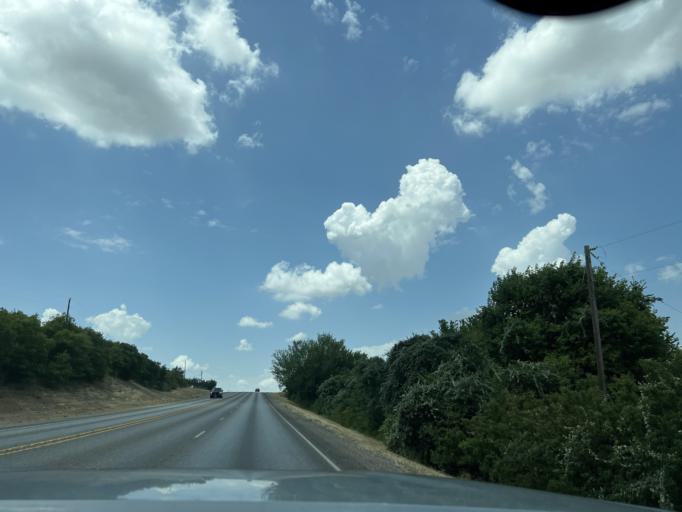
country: US
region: Texas
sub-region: Parker County
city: Springtown
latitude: 32.9333
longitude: -97.7016
